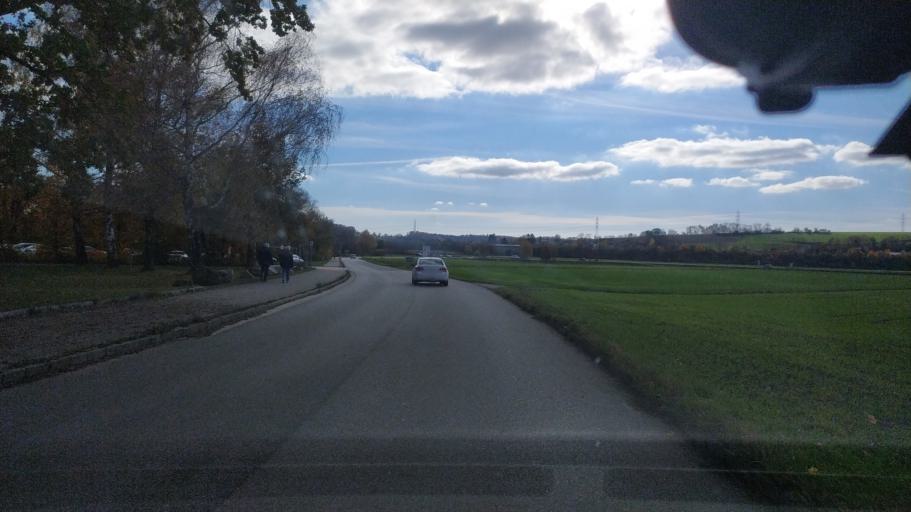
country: AT
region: Upper Austria
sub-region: Politischer Bezirk Linz-Land
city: Sankt Florian
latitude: 48.2385
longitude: 14.3751
